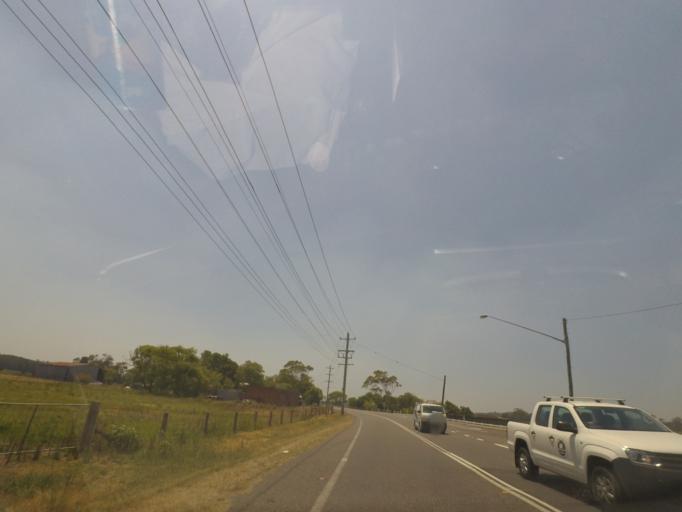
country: AU
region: New South Wales
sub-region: Port Stephens Shire
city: Medowie
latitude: -32.8024
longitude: 151.8861
